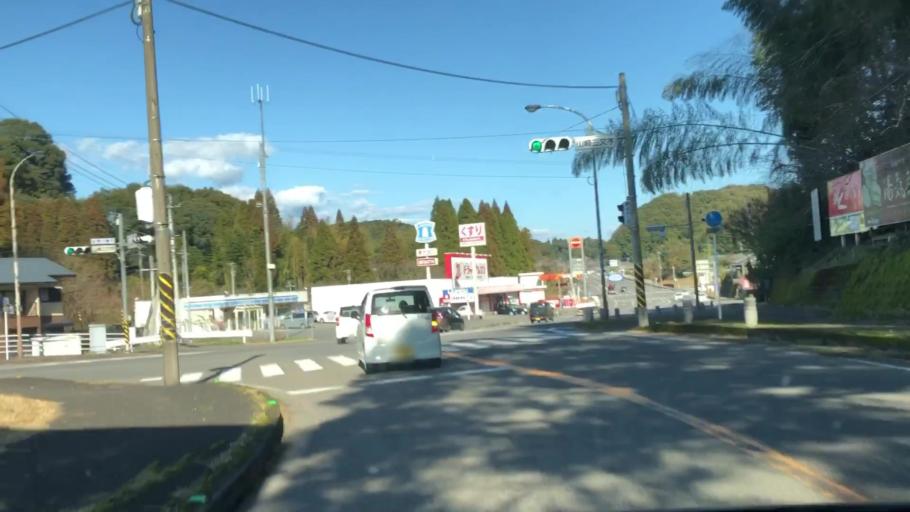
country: JP
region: Kagoshima
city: Satsumasendai
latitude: 31.8676
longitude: 130.4317
